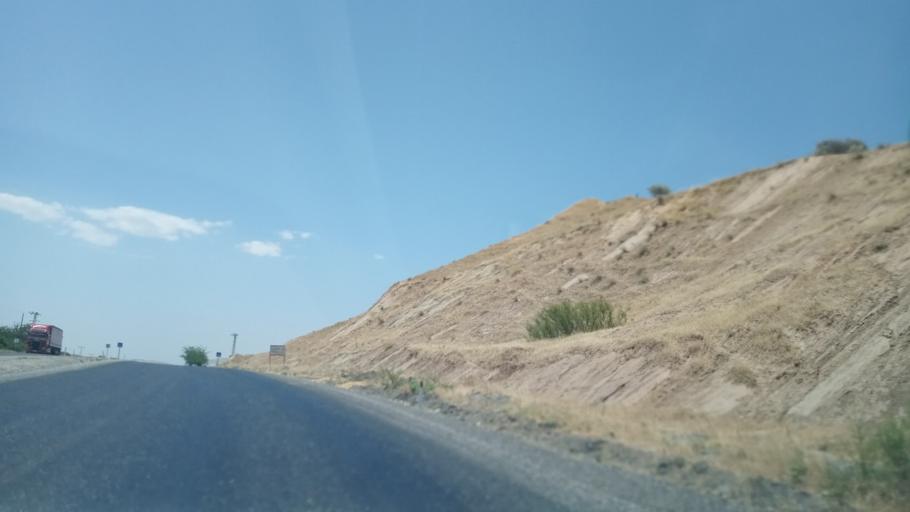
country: TR
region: Batman
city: Kozluk
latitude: 38.1734
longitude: 41.4452
